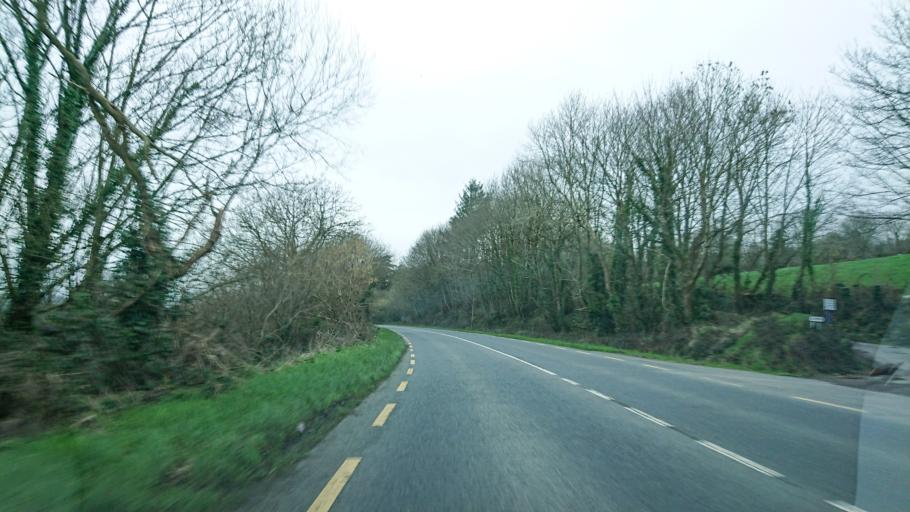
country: IE
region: Munster
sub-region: County Cork
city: Bandon
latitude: 51.7467
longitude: -8.7688
